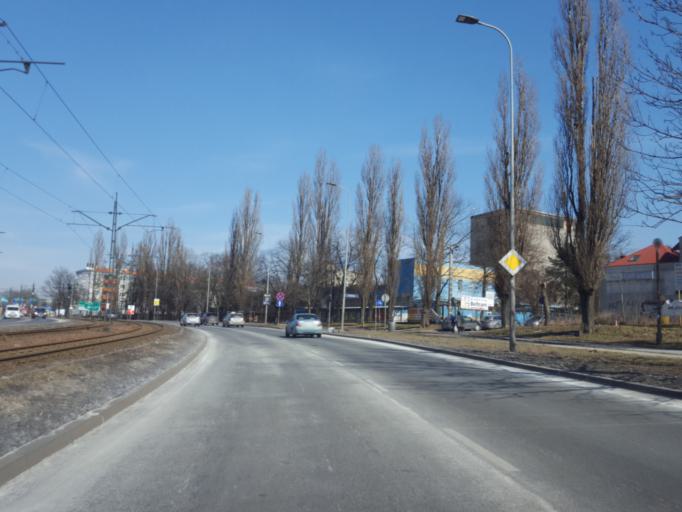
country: PL
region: Lesser Poland Voivodeship
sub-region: Krakow
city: Krakow
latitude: 50.0704
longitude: 20.0155
